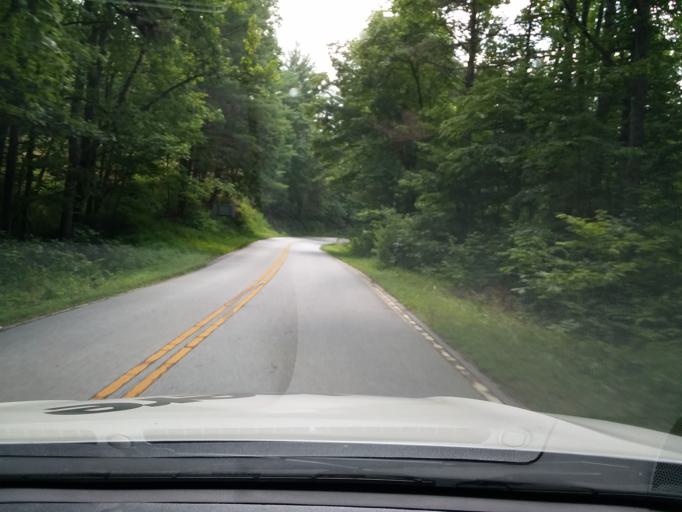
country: US
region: Georgia
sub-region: Rabun County
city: Mountain City
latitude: 35.0001
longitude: -83.1988
